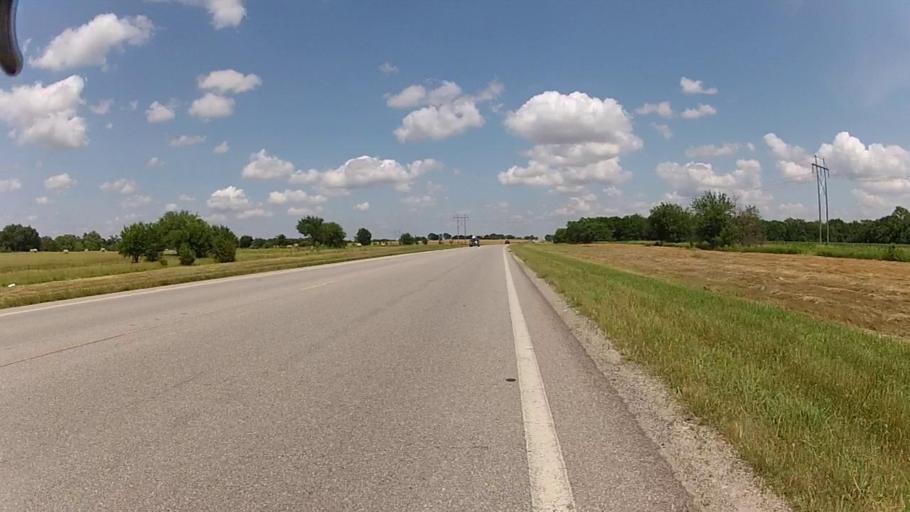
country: US
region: Kansas
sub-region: Labette County
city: Altamont
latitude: 37.1938
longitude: -95.2611
